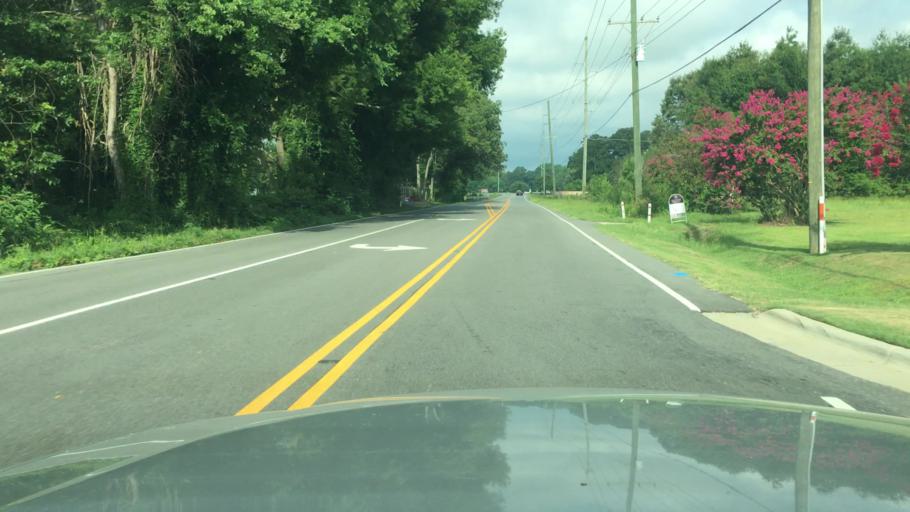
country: US
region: North Carolina
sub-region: Cumberland County
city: Hope Mills
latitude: 34.9497
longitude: -78.8545
